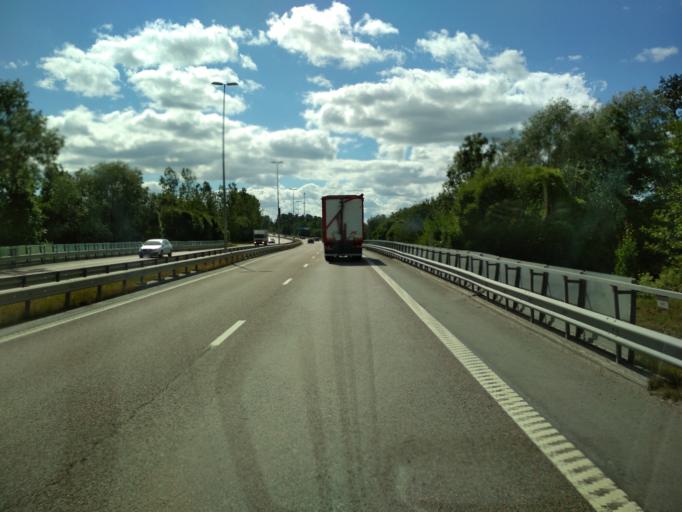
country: SE
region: Uppsala
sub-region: Uppsala Kommun
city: Gamla Uppsala
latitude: 59.8763
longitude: 17.6073
